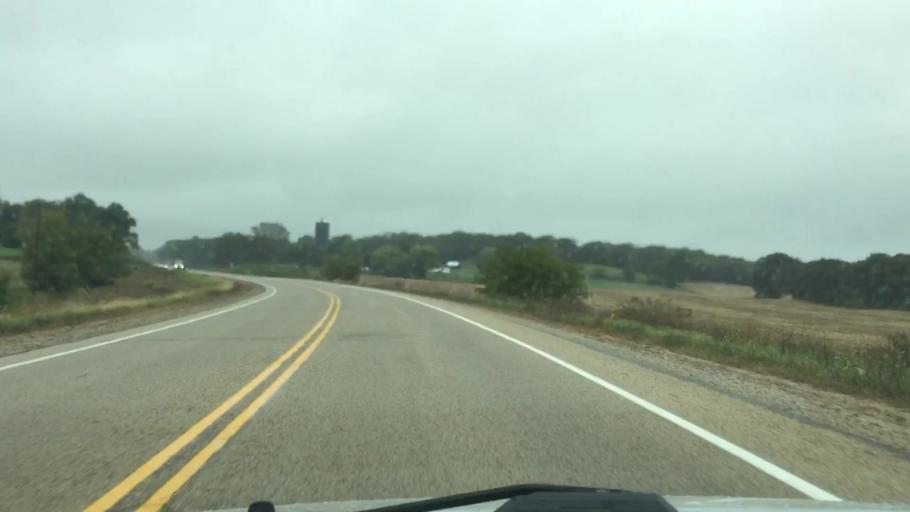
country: US
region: Wisconsin
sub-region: Jefferson County
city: Palmyra
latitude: 42.8853
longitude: -88.5650
